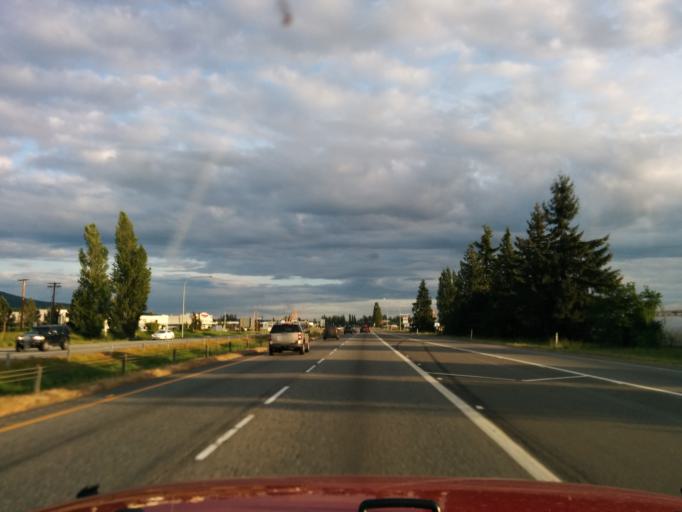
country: US
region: Washington
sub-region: Skagit County
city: Mount Vernon
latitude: 48.3969
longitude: -122.3307
